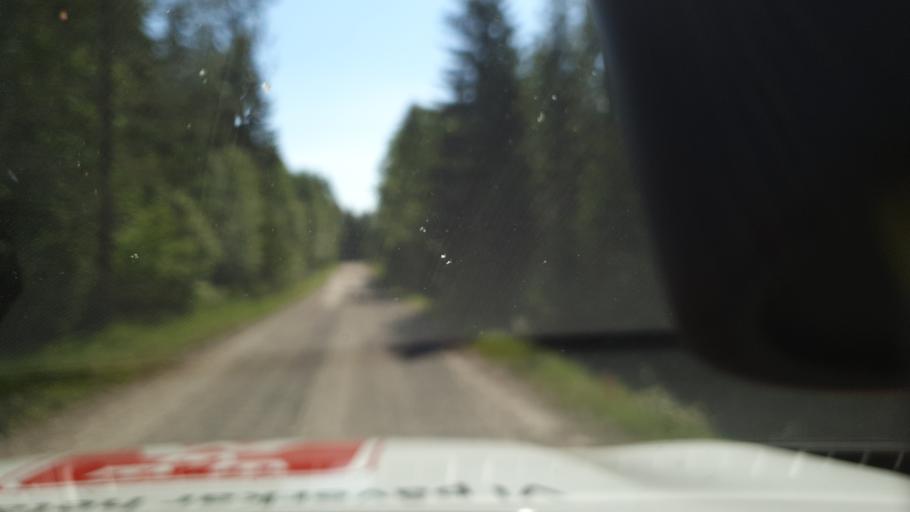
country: SE
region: Vaesterbotten
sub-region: Robertsfors Kommun
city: Robertsfors
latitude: 64.2257
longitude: 21.0671
